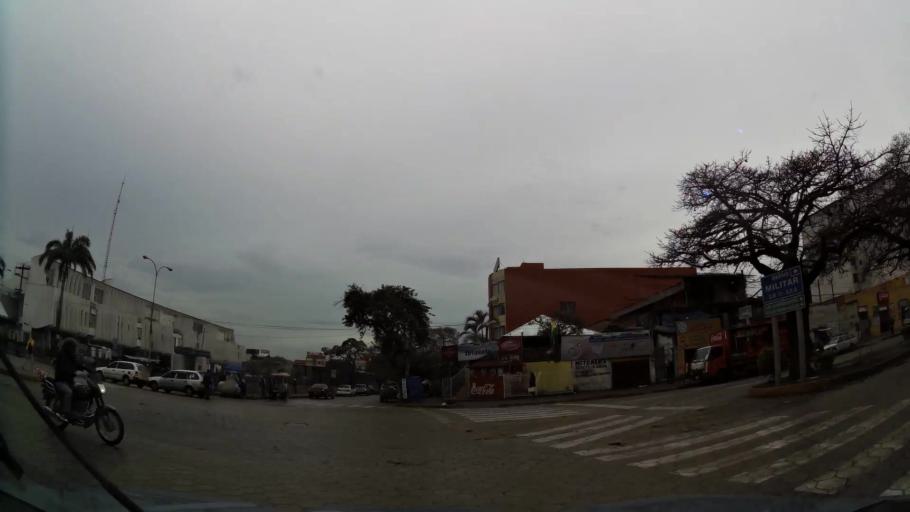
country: BO
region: Santa Cruz
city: Santa Cruz de la Sierra
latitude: -17.7932
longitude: -63.1858
